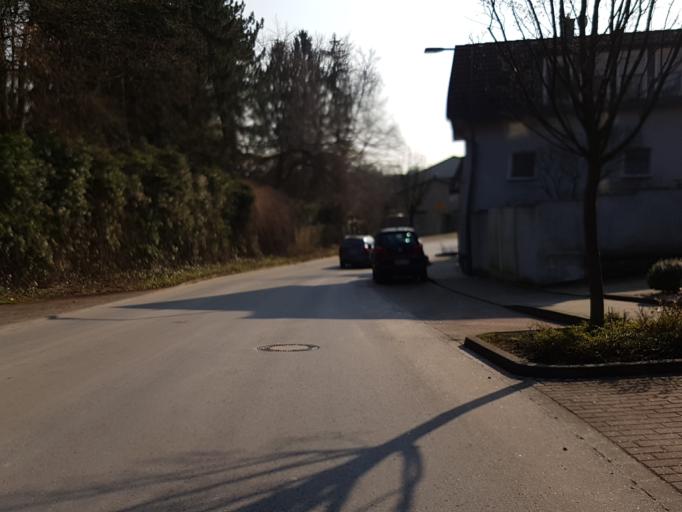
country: DE
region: North Rhine-Westphalia
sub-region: Regierungsbezirk Koln
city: Wurselen
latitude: 50.7893
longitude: 6.1566
